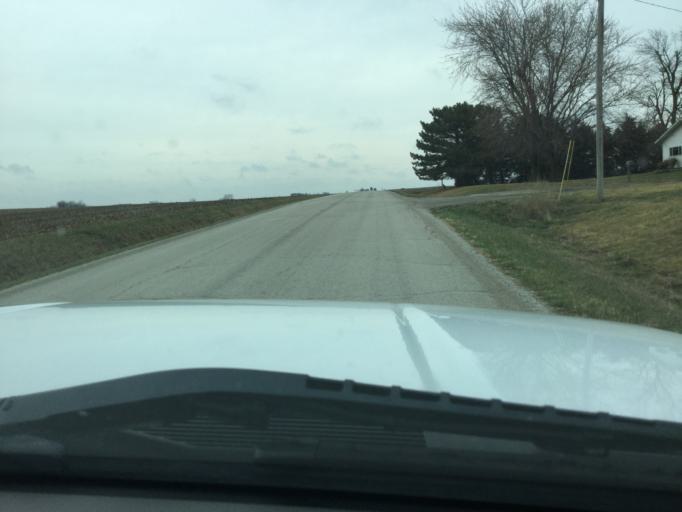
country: US
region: Kansas
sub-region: Nemaha County
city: Sabetha
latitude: 39.8441
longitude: -95.7142
